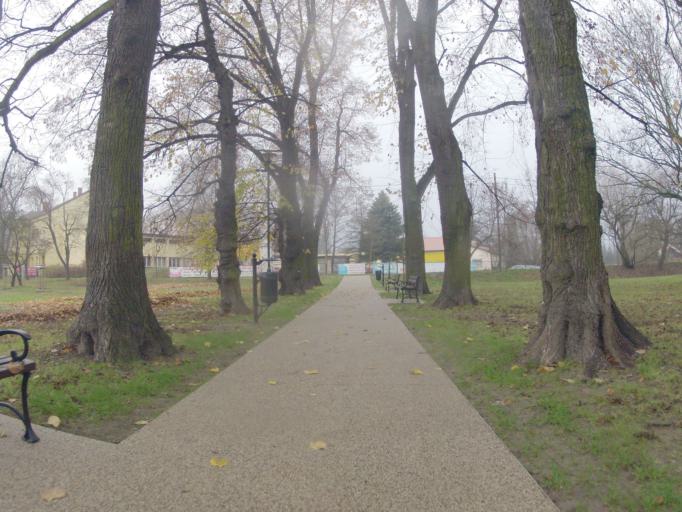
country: PL
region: Lesser Poland Voivodeship
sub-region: Powiat krakowski
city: Zielonki
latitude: 50.0940
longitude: 19.9398
